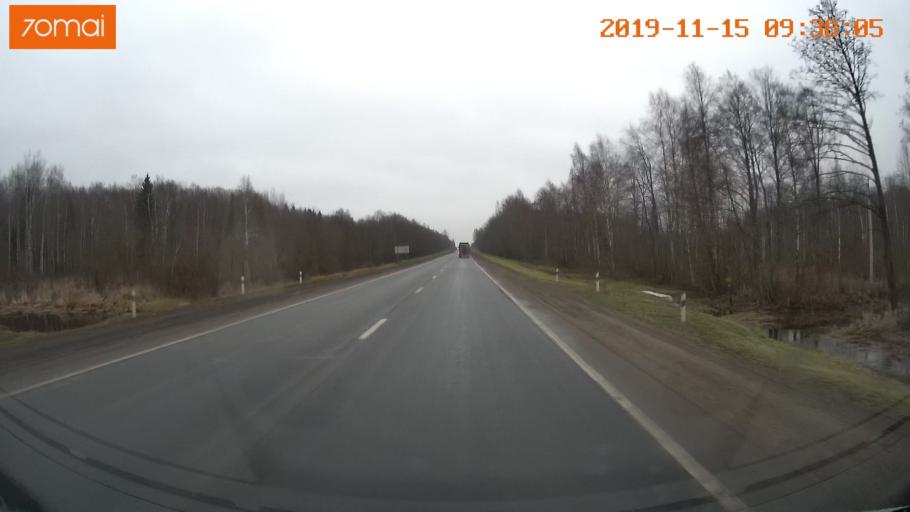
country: RU
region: Vologda
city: Sheksna
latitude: 59.2351
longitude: 38.4489
